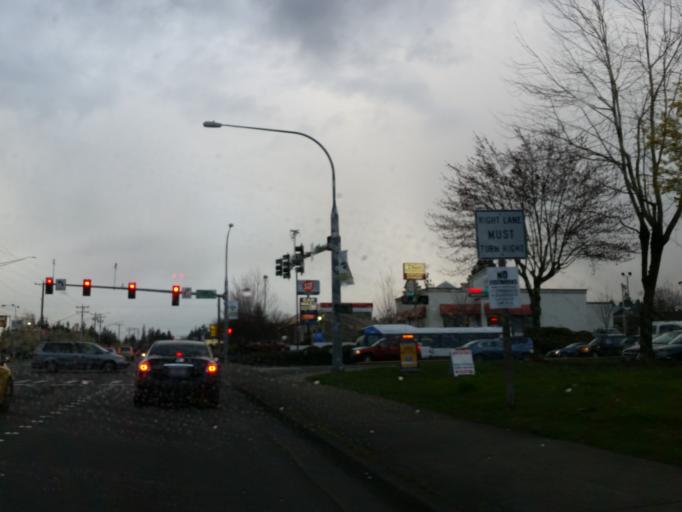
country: US
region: Washington
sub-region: Snohomish County
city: Alderwood Manor
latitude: 47.8169
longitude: -122.2922
